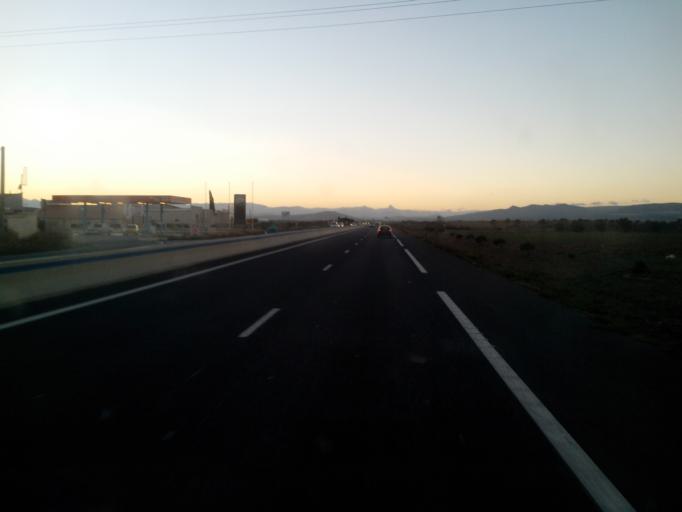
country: FR
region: Languedoc-Roussillon
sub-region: Departement des Pyrenees-Orientales
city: Saint-Hippolyte
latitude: 42.7775
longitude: 2.9527
